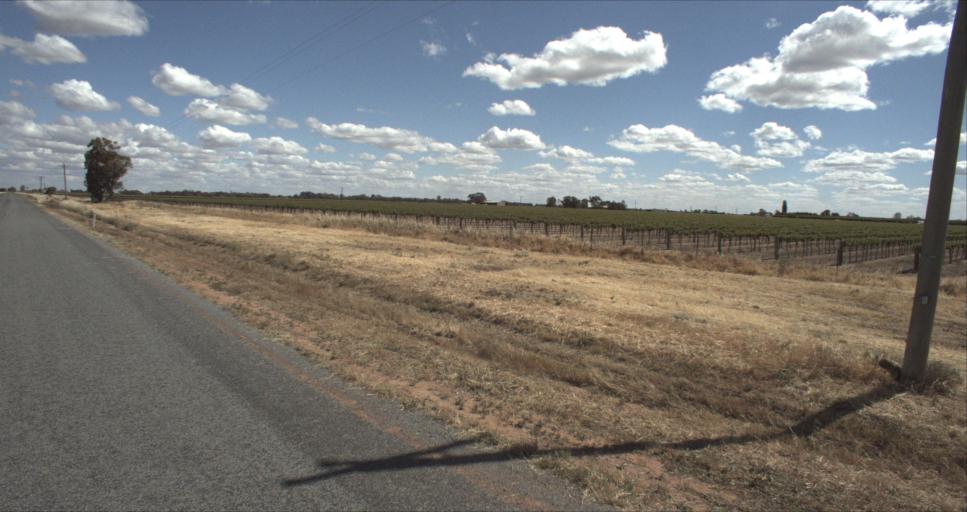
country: AU
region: New South Wales
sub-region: Leeton
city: Leeton
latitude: -34.4923
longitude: 146.2470
